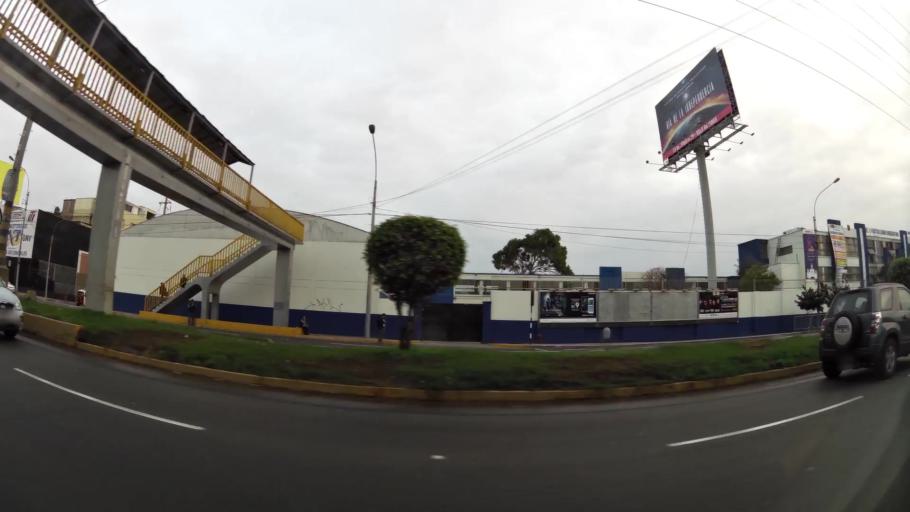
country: PE
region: Lima
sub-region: Lima
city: San Isidro
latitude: -12.0812
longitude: -77.0738
